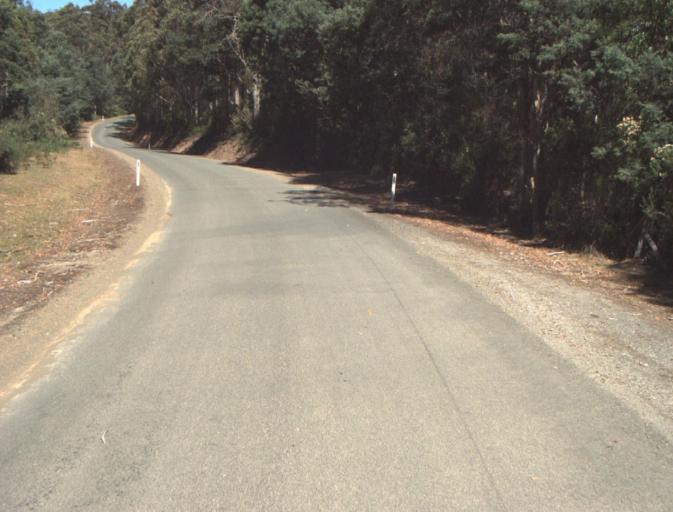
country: AU
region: Tasmania
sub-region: Dorset
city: Scottsdale
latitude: -41.3141
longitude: 147.4017
